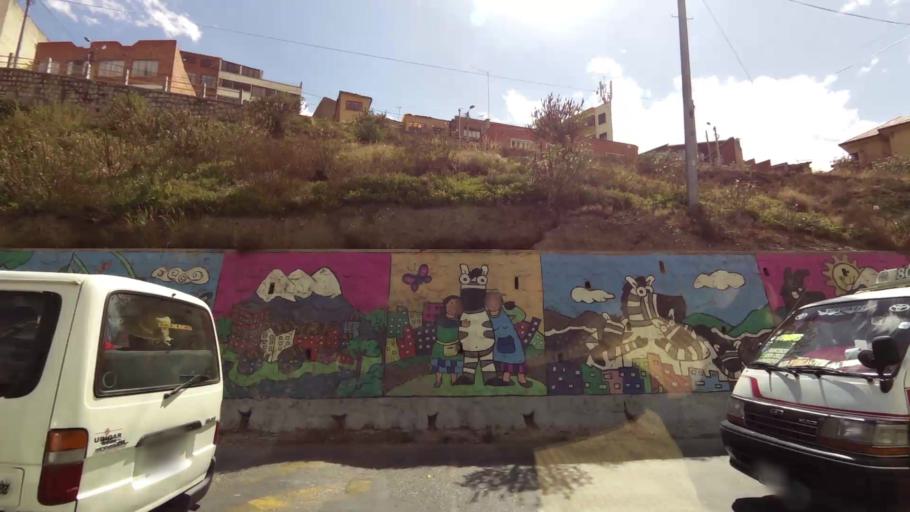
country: BO
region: La Paz
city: La Paz
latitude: -16.4936
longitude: -68.1252
